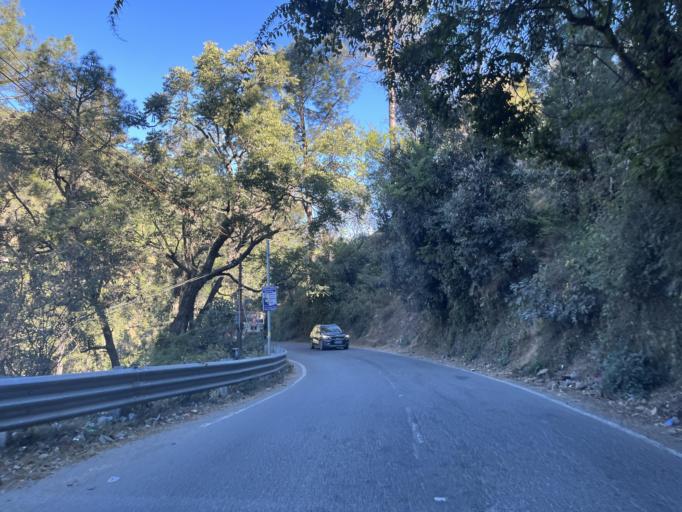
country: IN
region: Uttarakhand
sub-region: Naini Tal
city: Bhowali
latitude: 29.4060
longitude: 79.5149
